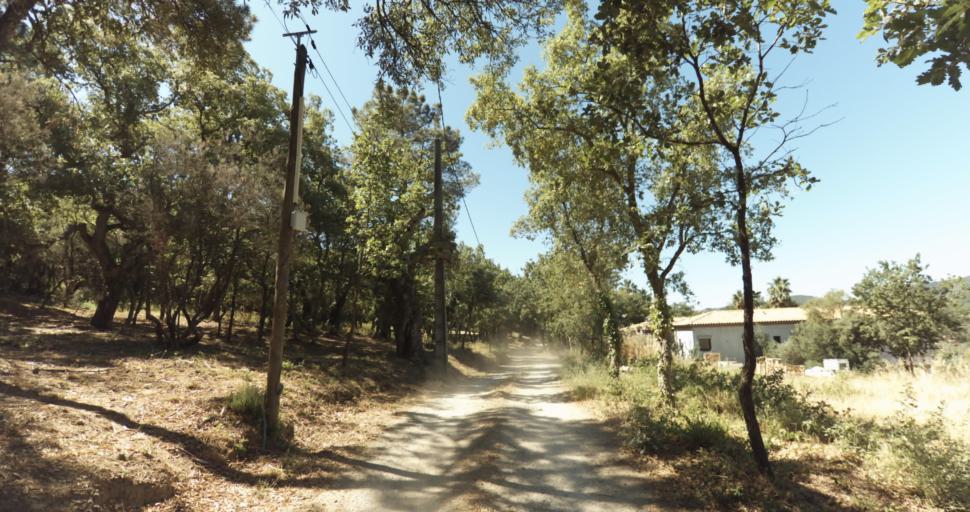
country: FR
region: Provence-Alpes-Cote d'Azur
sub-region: Departement du Var
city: Gassin
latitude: 43.2365
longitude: 6.5791
